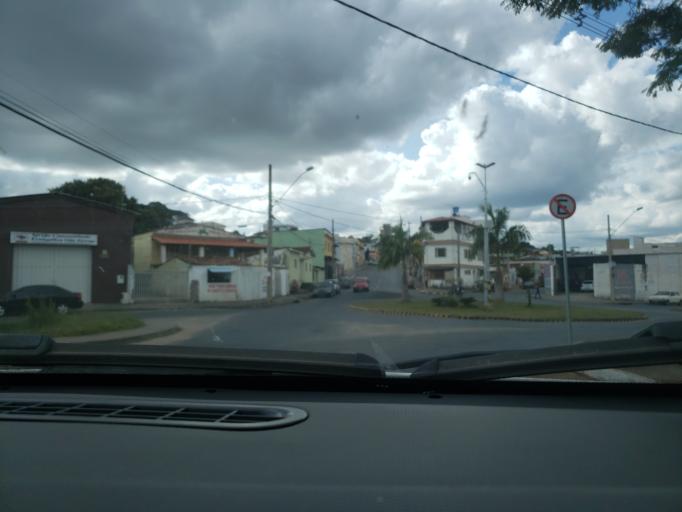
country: BR
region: Minas Gerais
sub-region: Campo Belo
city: Campo Belo
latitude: -20.9041
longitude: -45.2787
